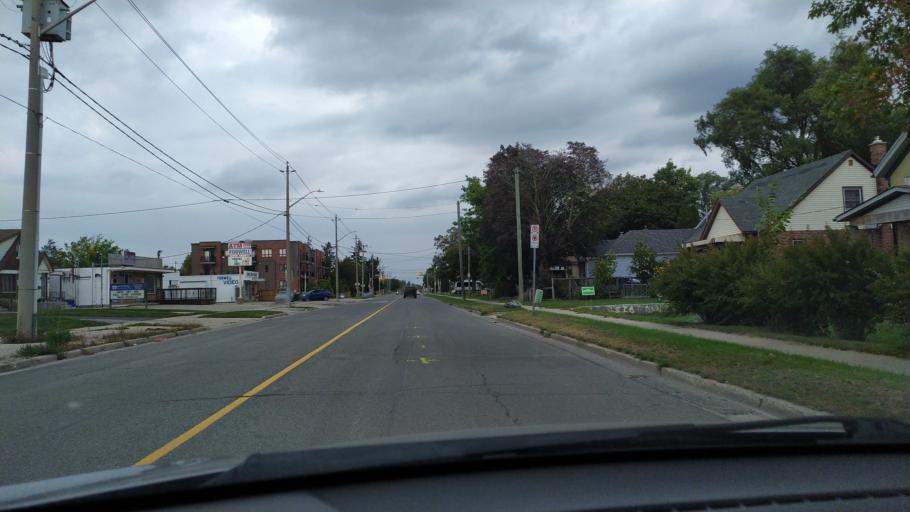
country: CA
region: Ontario
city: Waterloo
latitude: 43.4694
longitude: -80.4843
